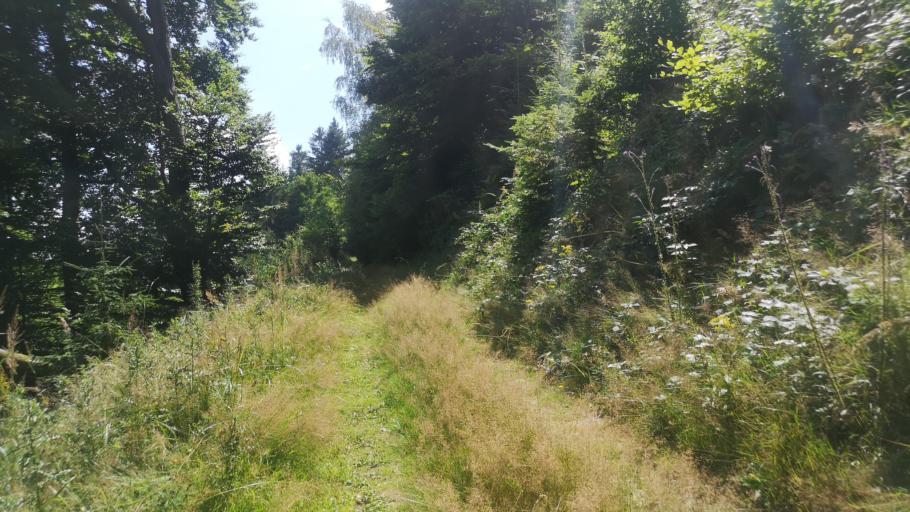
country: SK
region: Zilinsky
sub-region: Okres Zilina
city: Vrutky
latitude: 49.0964
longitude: 18.8547
